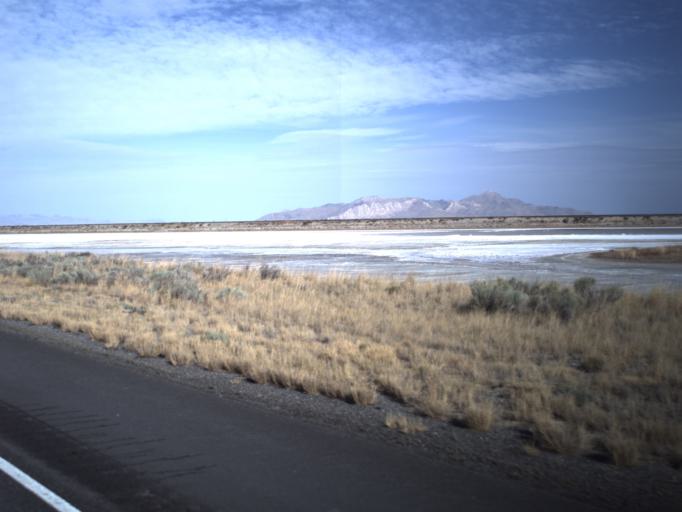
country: US
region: Utah
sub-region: Tooele County
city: Stansbury park
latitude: 40.6646
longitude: -112.3615
